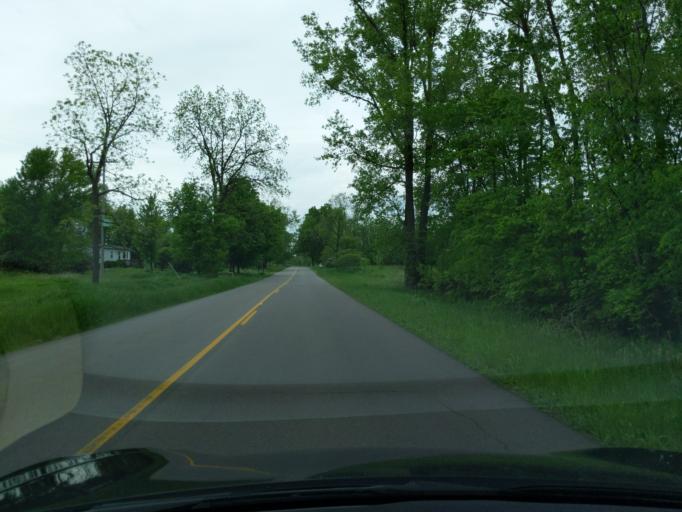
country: US
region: Michigan
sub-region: Ingham County
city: Leslie
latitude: 42.4126
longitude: -84.3531
